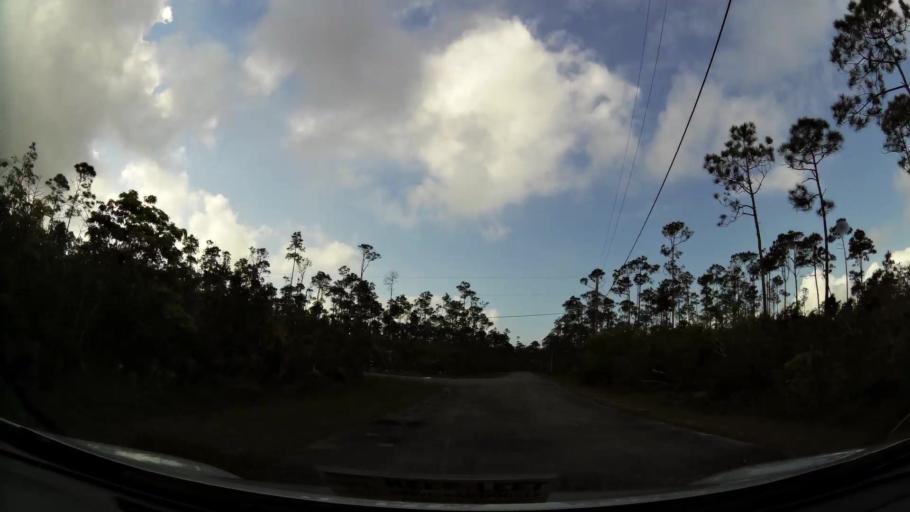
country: BS
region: Freeport
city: Lucaya
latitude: 26.5876
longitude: -78.5496
